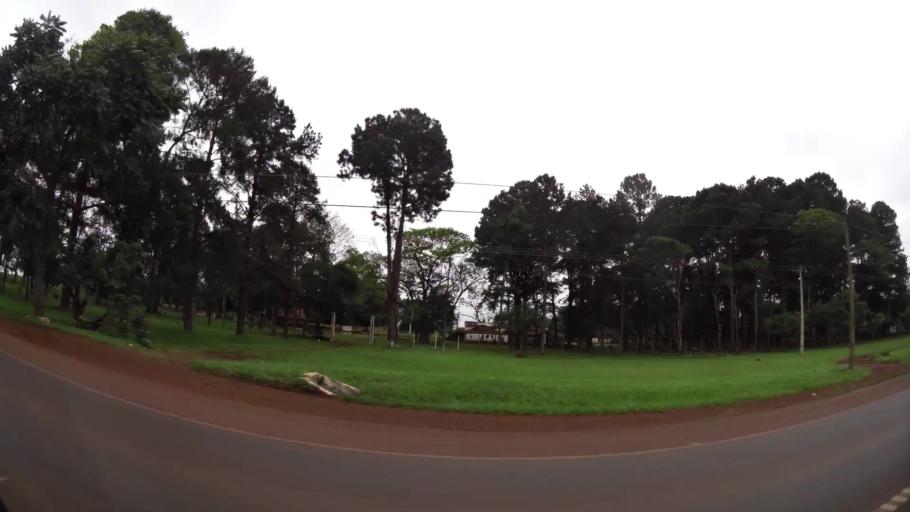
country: PY
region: Alto Parana
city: Colonia Yguazu
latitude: -25.4883
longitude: -54.8199
